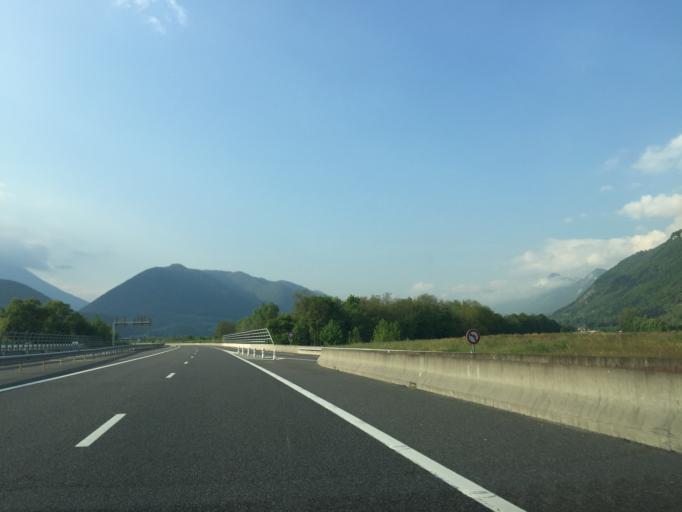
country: FR
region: Rhone-Alpes
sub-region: Departement de l'Isere
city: Vif
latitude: 45.0744
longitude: 5.6794
